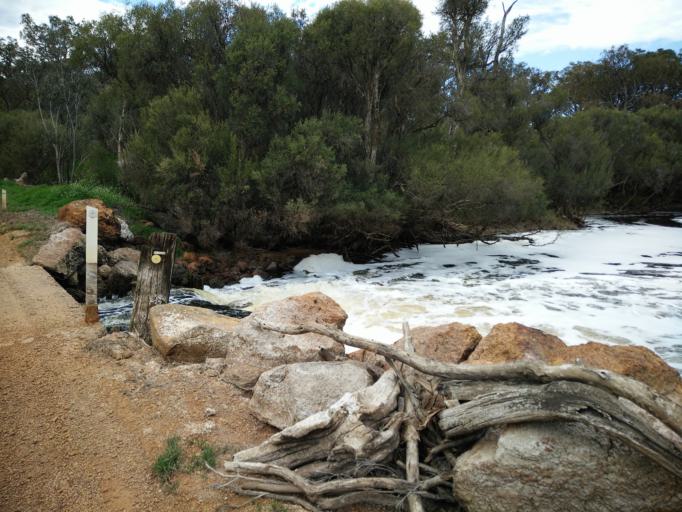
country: AU
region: Western Australia
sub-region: Boyup Brook
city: Boyup Brook
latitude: -33.8572
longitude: 116.3777
